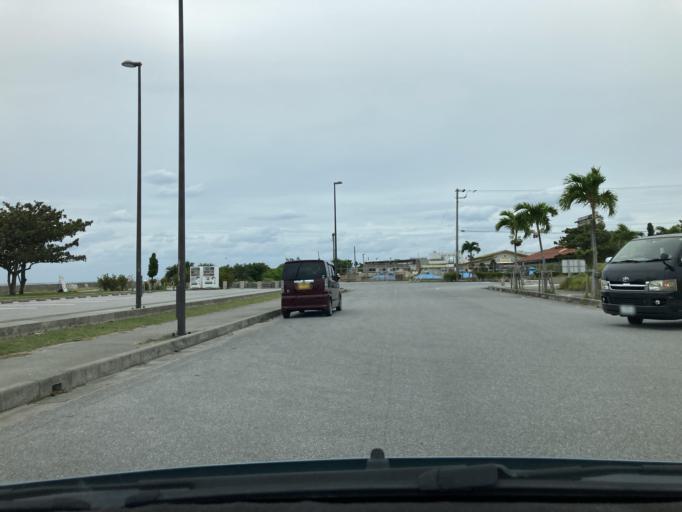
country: JP
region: Okinawa
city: Itoman
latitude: 26.1348
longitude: 127.6515
